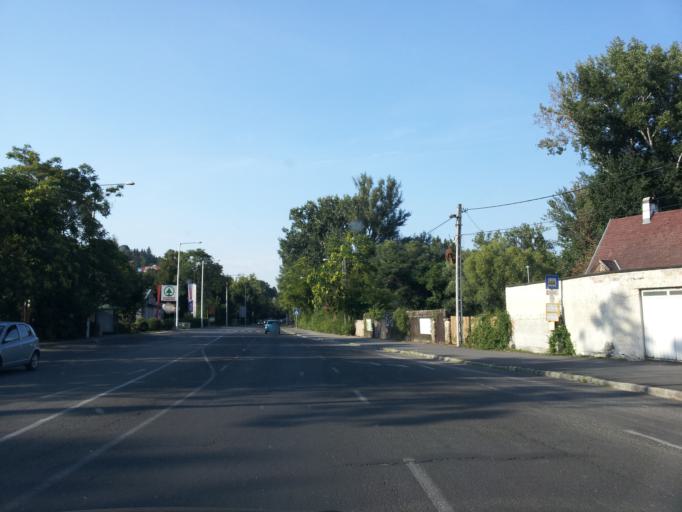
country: HU
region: Pest
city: Szentendre
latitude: 47.6788
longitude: 19.0799
